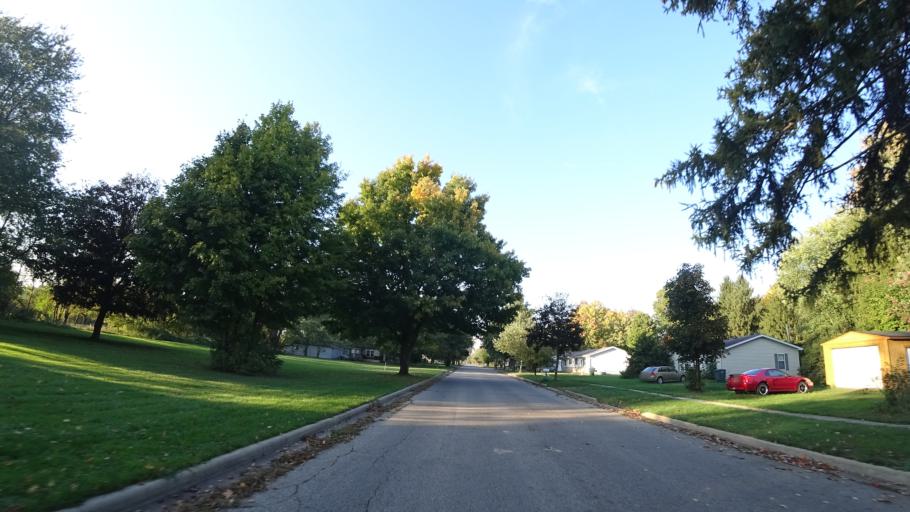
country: US
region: Michigan
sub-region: Saint Joseph County
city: Three Rivers
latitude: 41.9453
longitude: -85.6444
